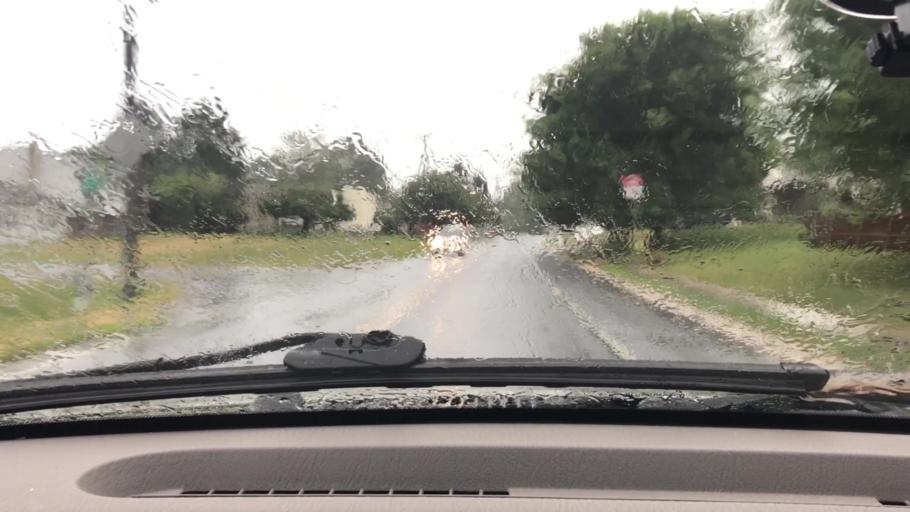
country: US
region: Pennsylvania
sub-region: Lancaster County
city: Elizabethtown
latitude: 40.1293
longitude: -76.6133
